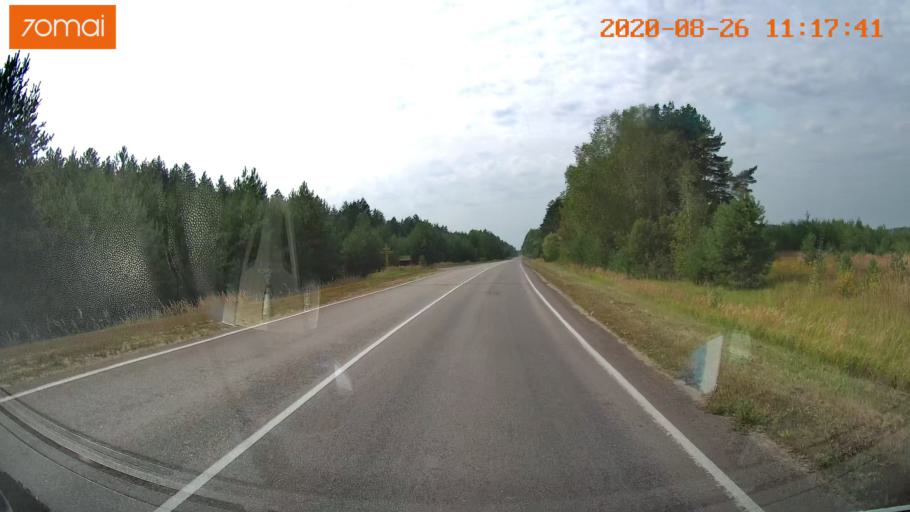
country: RU
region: Rjazan
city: Shilovo
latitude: 54.4166
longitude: 41.1086
